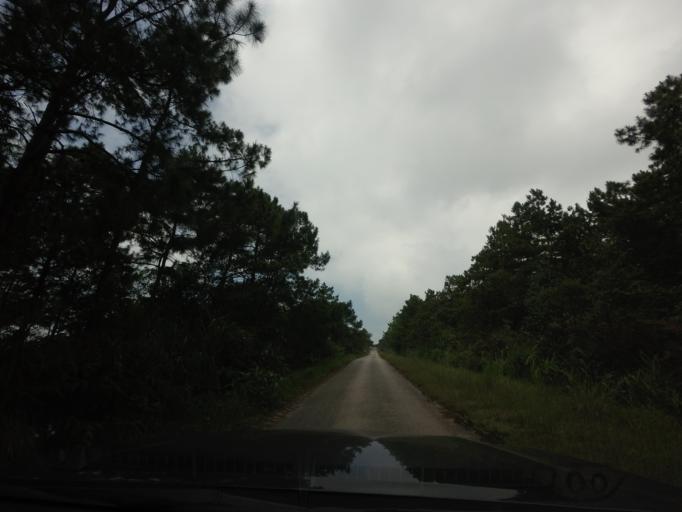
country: TH
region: Loei
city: Phu Ruea
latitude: 17.5059
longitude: 101.3478
